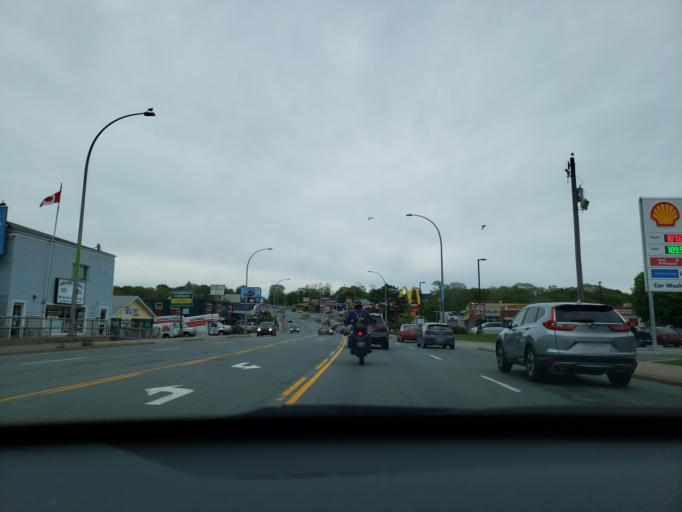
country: CA
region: Nova Scotia
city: Dartmouth
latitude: 44.6819
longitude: -63.5392
